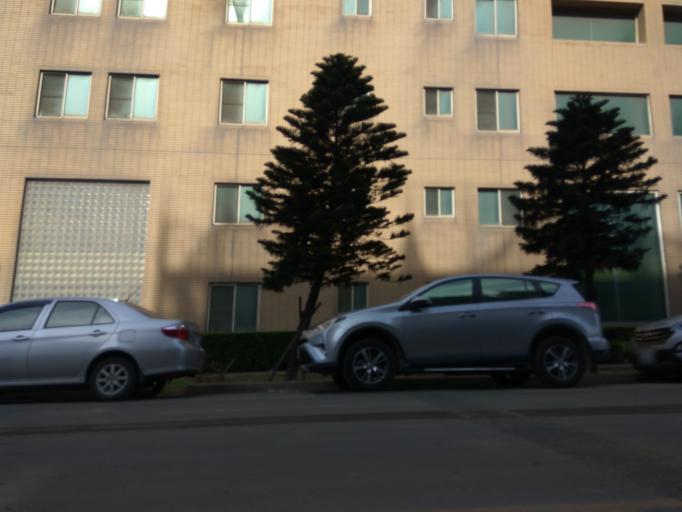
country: TW
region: Taiwan
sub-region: Hsinchu
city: Zhubei
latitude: 25.0356
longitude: 121.0580
